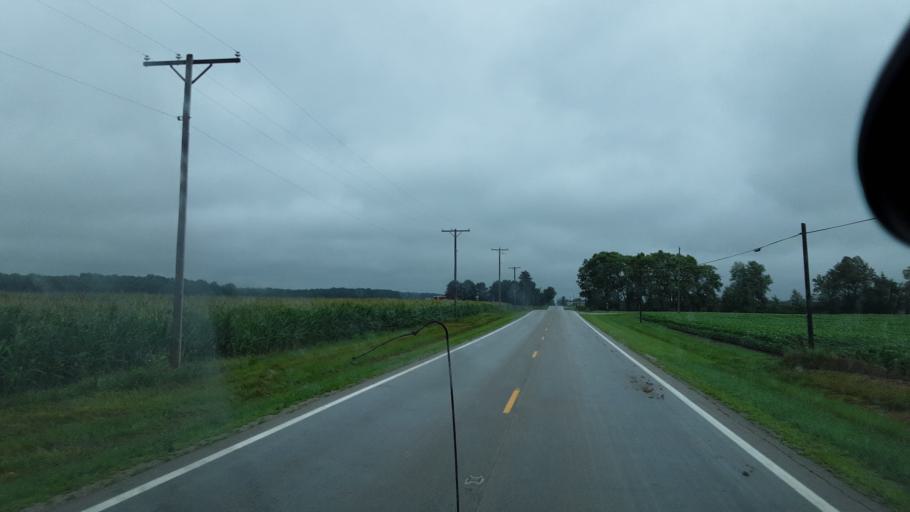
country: US
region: Ohio
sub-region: Mercer County
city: Rockford
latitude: 40.7426
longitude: -84.7418
